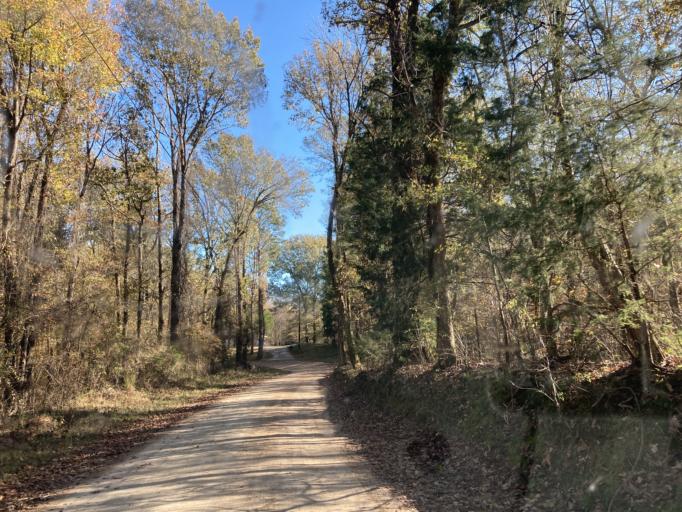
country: US
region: Mississippi
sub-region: Yazoo County
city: Yazoo City
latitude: 32.6978
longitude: -90.4929
